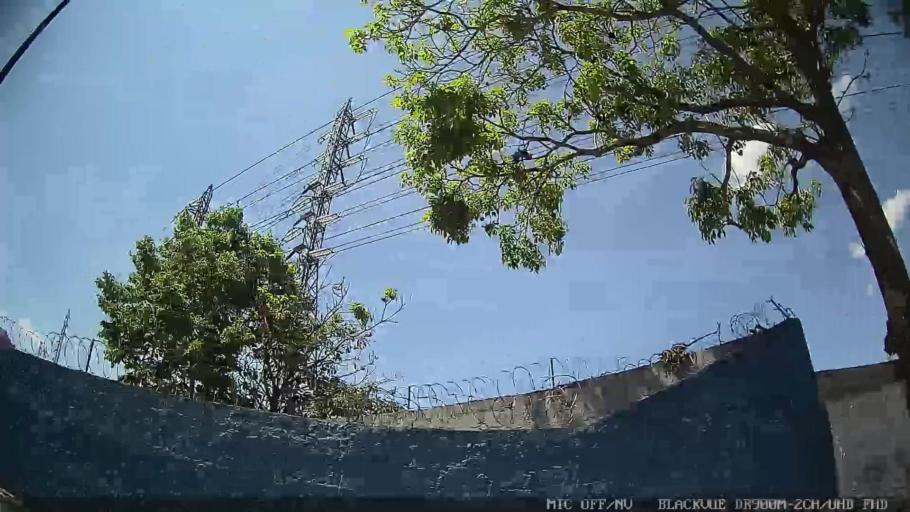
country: BR
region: Sao Paulo
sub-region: Guarulhos
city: Guarulhos
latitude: -23.5170
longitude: -46.5157
